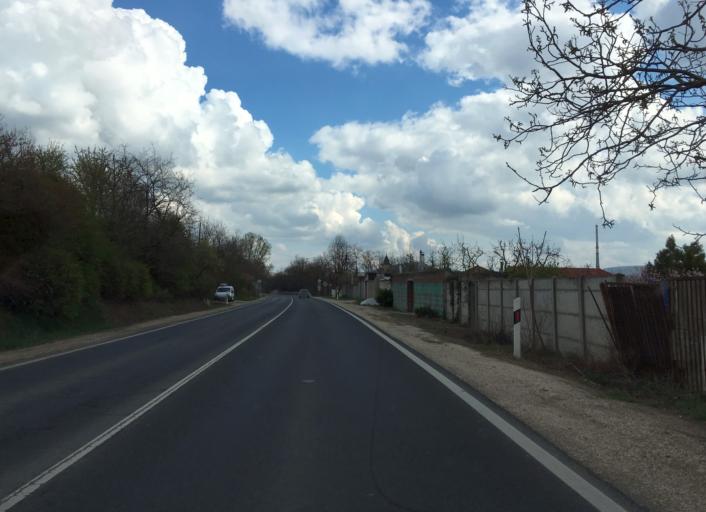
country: HU
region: Komarom-Esztergom
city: Tatabanya
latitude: 47.5749
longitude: 18.4140
